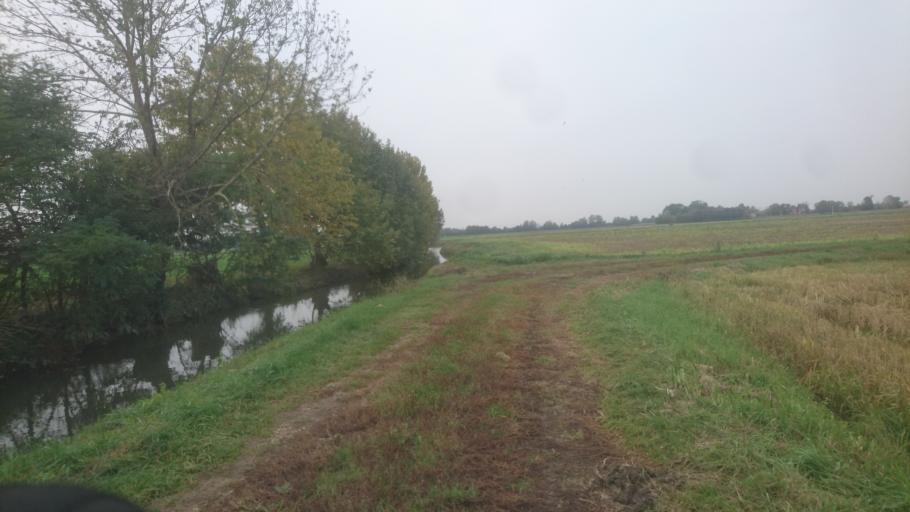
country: IT
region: Veneto
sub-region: Provincia di Vicenza
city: Grumolo delle Abbadesse
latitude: 45.5493
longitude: 11.6709
